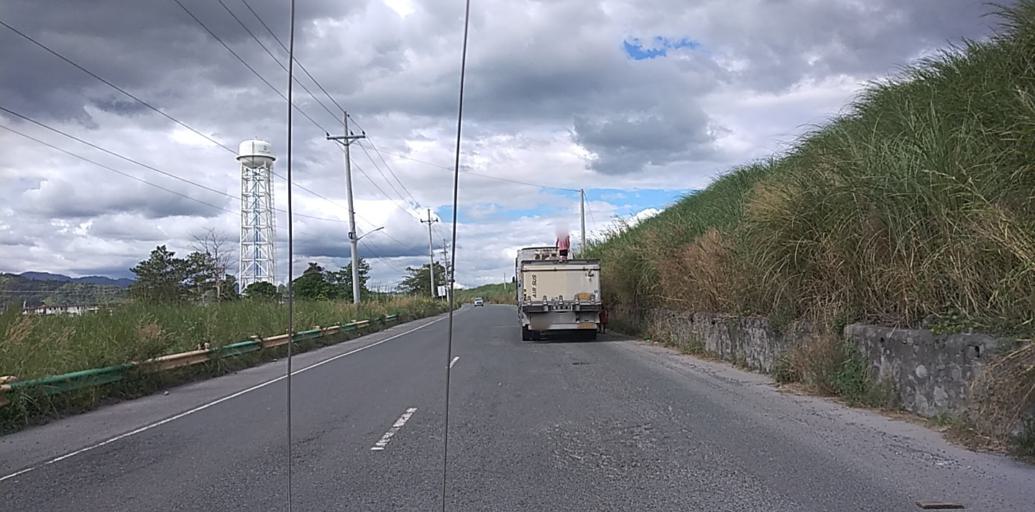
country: PH
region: Central Luzon
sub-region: Province of Pampanga
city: Dolores
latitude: 15.1105
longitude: 120.5184
